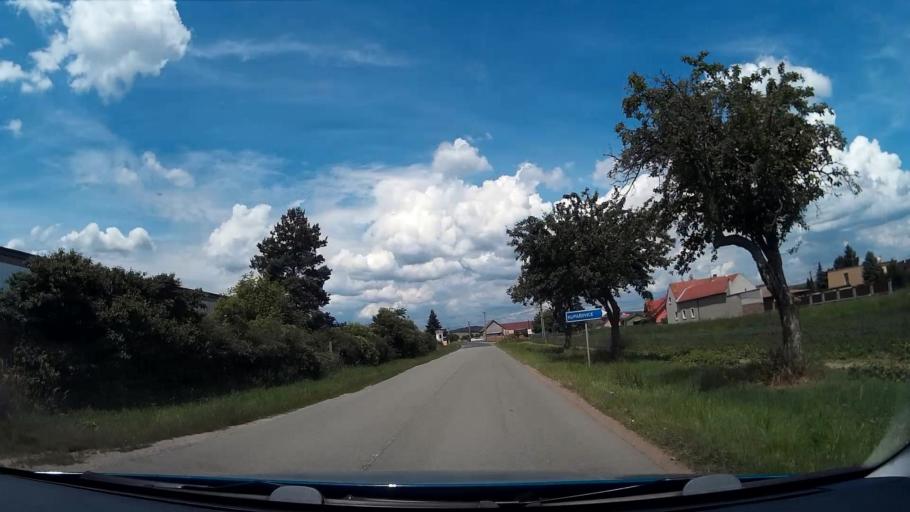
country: CZ
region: South Moravian
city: Dolni Kounice
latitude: 49.0402
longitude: 16.4846
